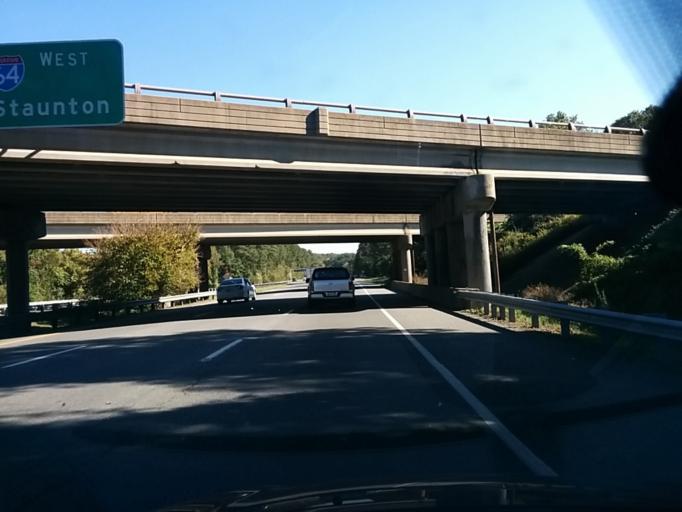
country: US
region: Virginia
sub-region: City of Charlottesville
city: Charlottesville
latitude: 38.0203
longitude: -78.5372
